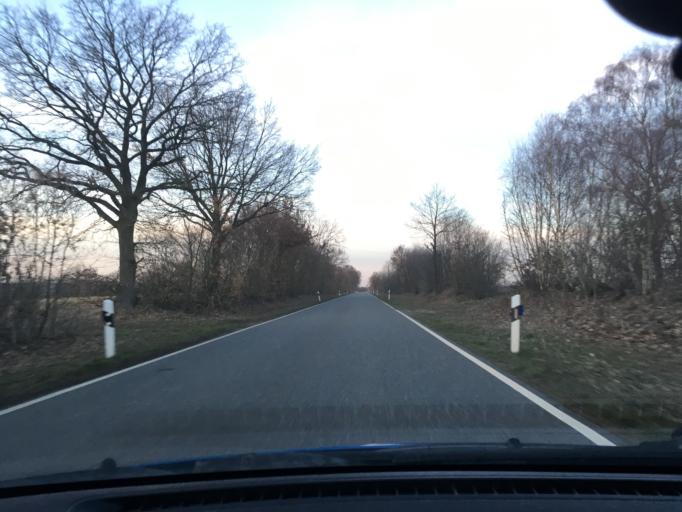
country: DE
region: Schleswig-Holstein
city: Besenthal
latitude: 53.5225
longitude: 10.7459
